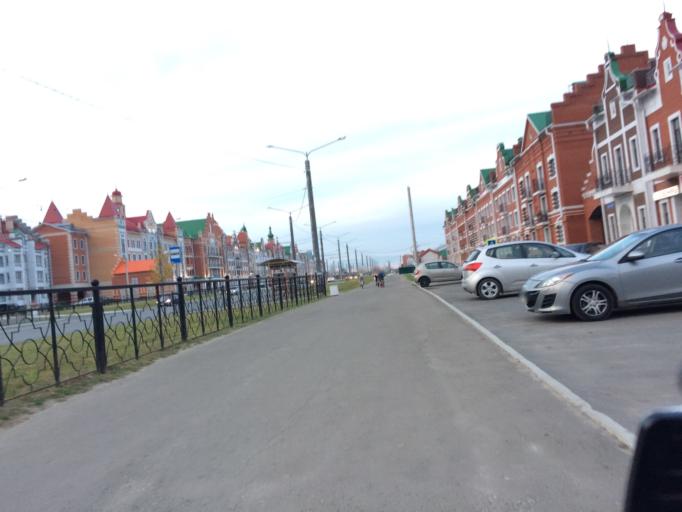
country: RU
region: Mariy-El
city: Yoshkar-Ola
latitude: 56.6325
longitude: 47.9102
